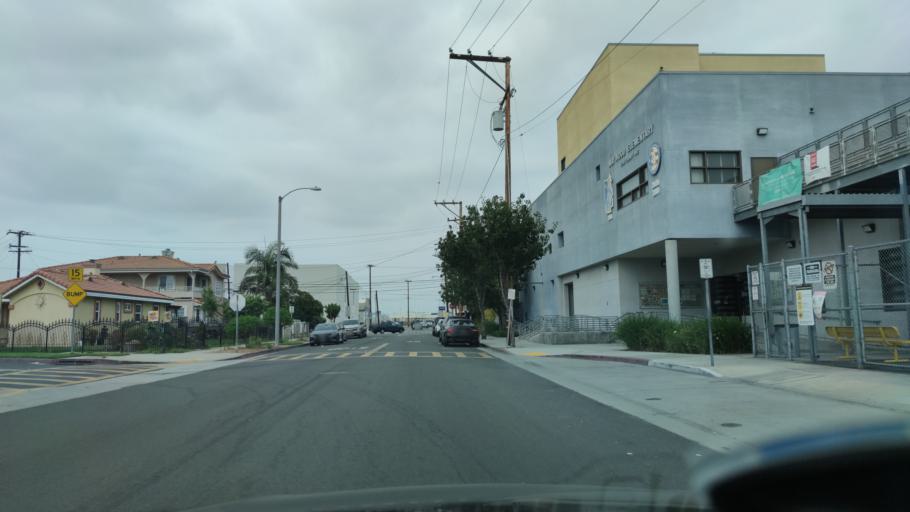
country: US
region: California
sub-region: Los Angeles County
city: Maywood
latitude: 33.9930
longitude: -118.1847
